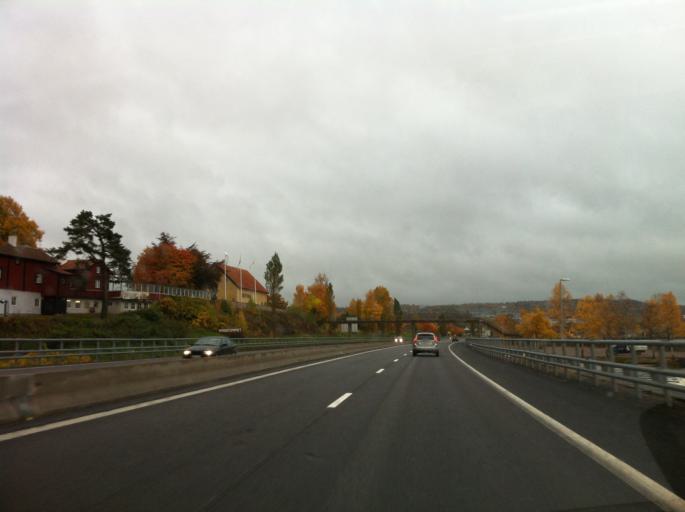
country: SE
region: Joenkoeping
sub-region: Jonkopings Kommun
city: Huskvarna
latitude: 57.8028
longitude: 14.2717
